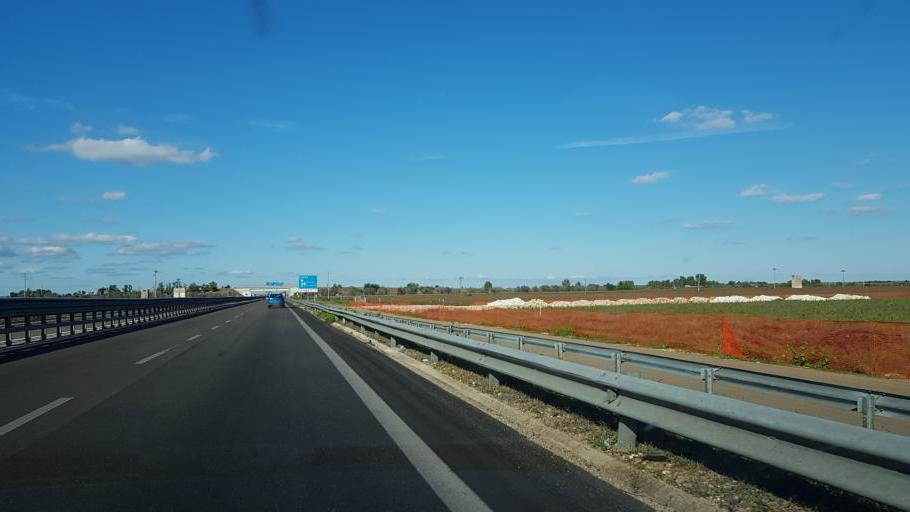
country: IT
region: Apulia
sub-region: Provincia di Lecce
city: Collemeto
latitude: 40.2527
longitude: 18.1166
